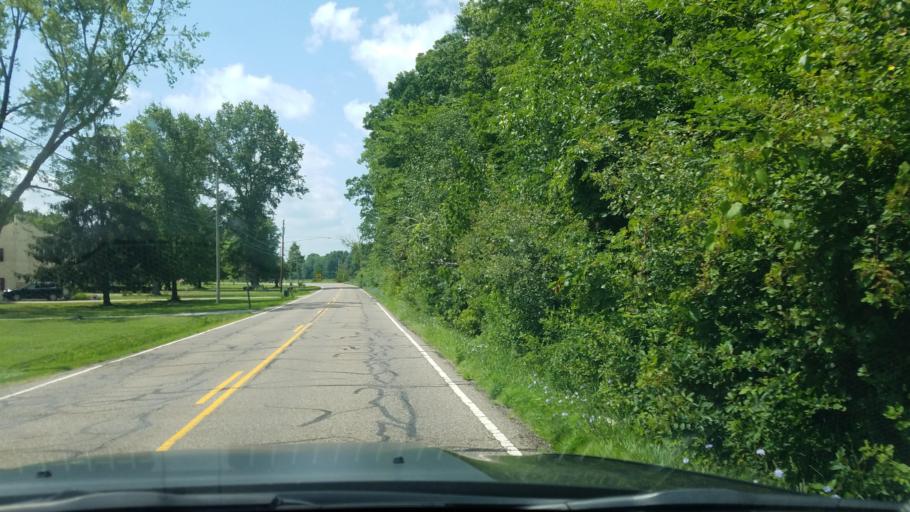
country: US
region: Ohio
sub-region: Trumbull County
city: Champion Heights
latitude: 41.2788
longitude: -80.8664
